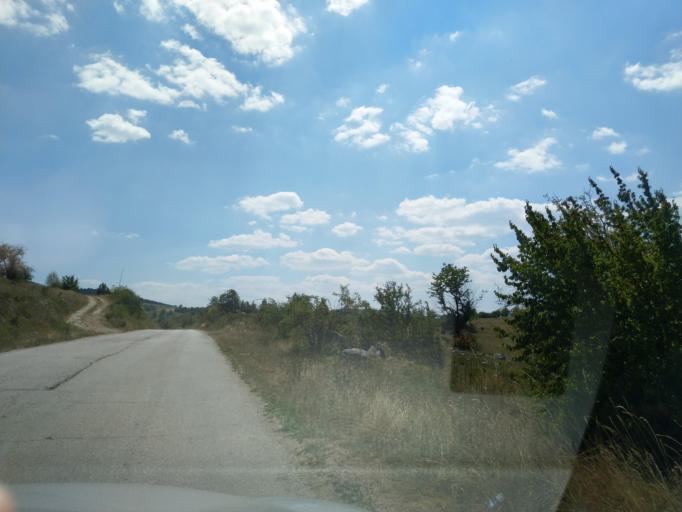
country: RS
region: Central Serbia
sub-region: Zlatiborski Okrug
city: Nova Varos
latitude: 43.4426
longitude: 19.9562
